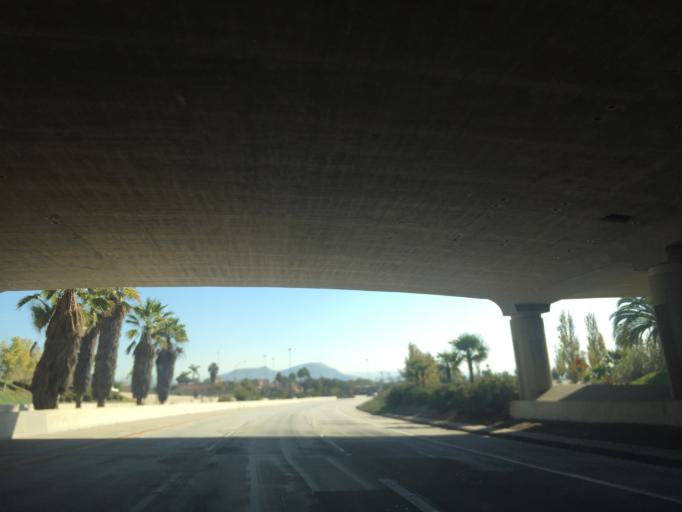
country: MX
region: Baja California
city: Tijuana
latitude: 32.5555
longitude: -116.9401
